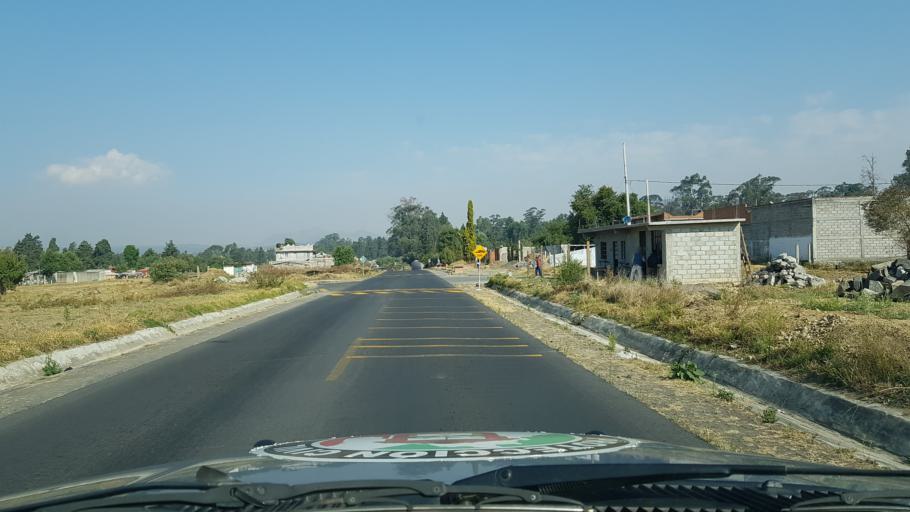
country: MX
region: Mexico
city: Ozumba de Alzate
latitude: 19.0497
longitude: -98.7806
